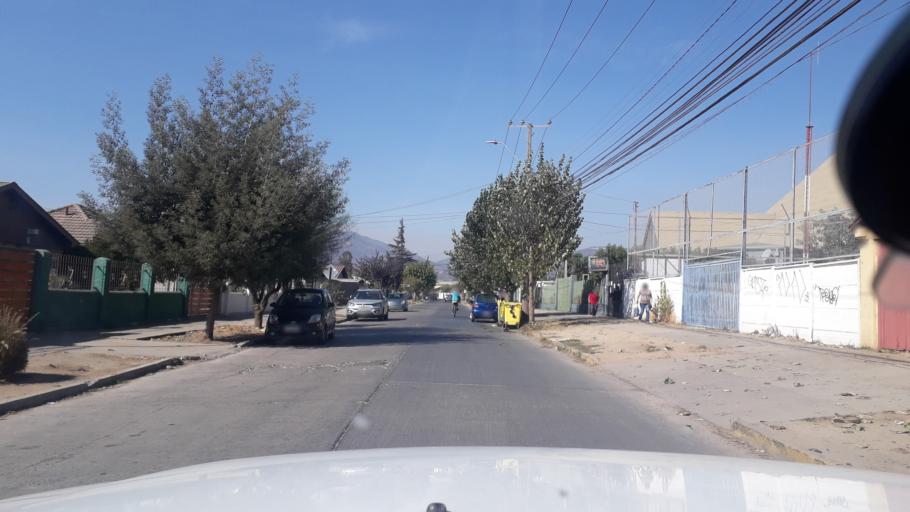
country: CL
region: Valparaiso
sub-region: Provincia de Marga Marga
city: Villa Alemana
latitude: -33.0436
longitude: -71.3542
